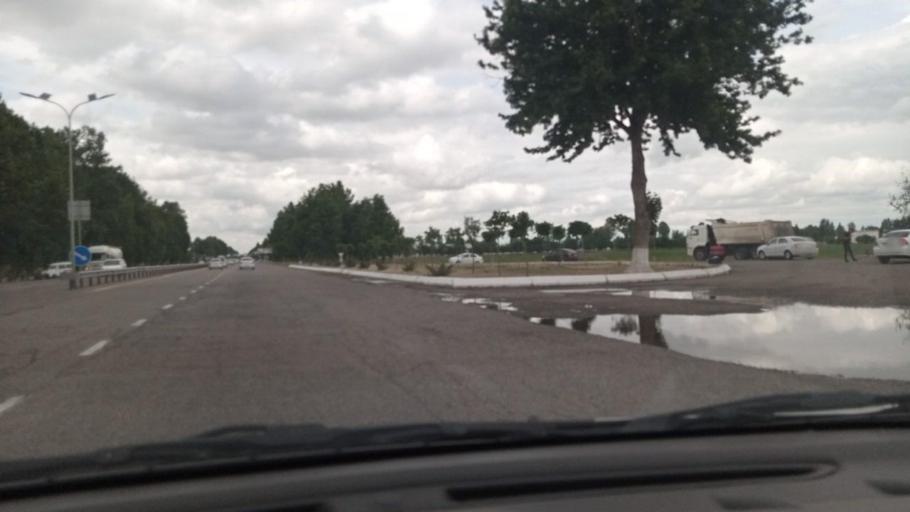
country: UZ
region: Toshkent Shahri
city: Bektemir
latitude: 41.2197
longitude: 69.4026
